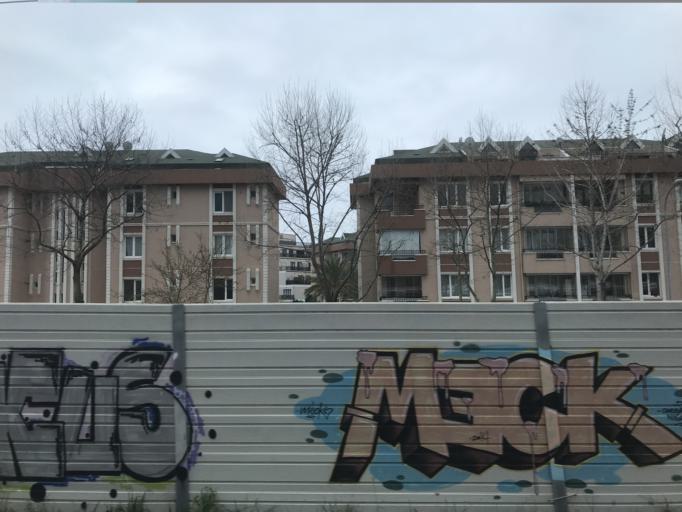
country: TR
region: Istanbul
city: Icmeler
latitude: 40.8391
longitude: 29.3093
